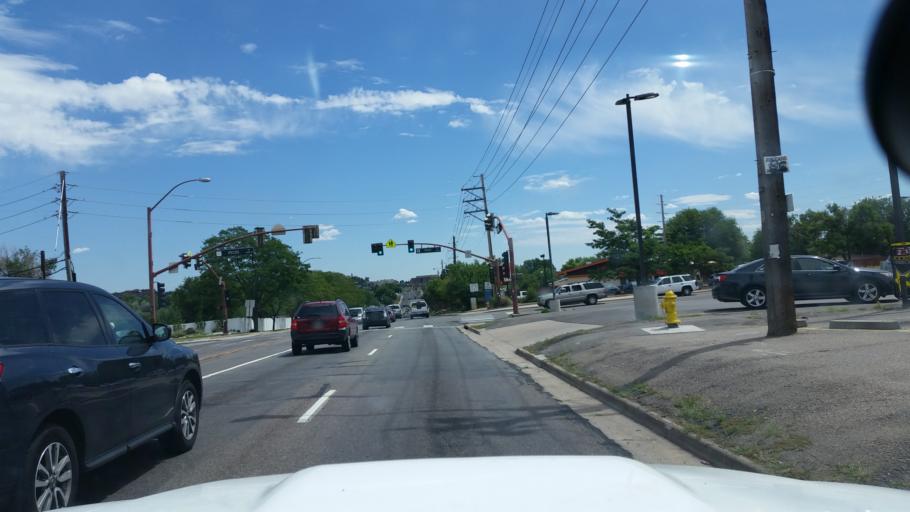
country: US
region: Colorado
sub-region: Adams County
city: Federal Heights
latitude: 39.8634
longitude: -105.0068
